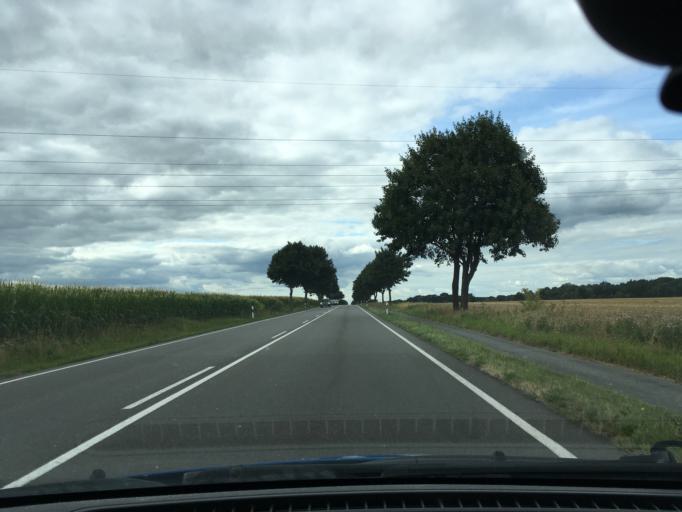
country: DE
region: Lower Saxony
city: Neu Wulmstorf
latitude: 53.4328
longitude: 9.7756
